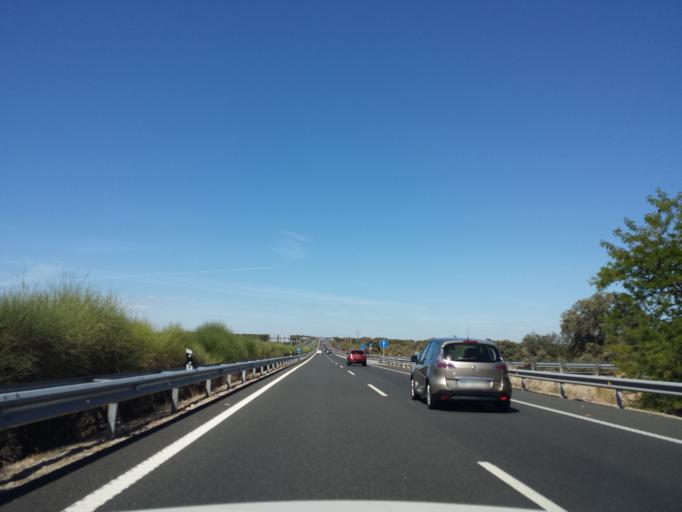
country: ES
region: Extremadura
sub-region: Provincia de Caceres
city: Peraleda de la Mata
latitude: 39.8907
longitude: -5.4311
